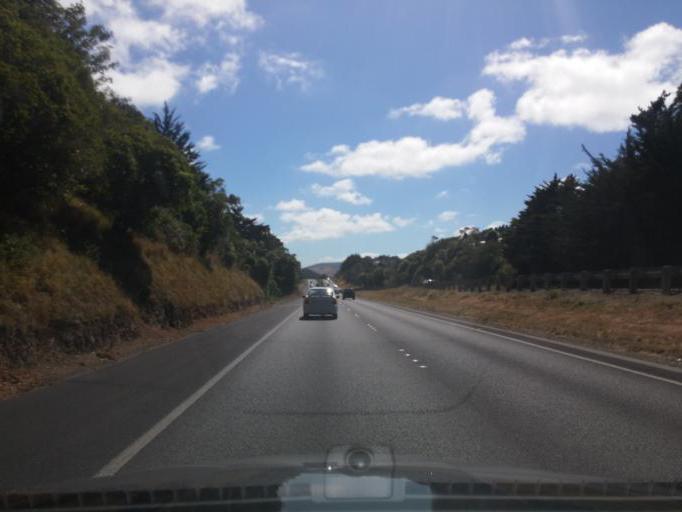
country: NZ
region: Wellington
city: Petone
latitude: -41.2128
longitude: 174.8142
